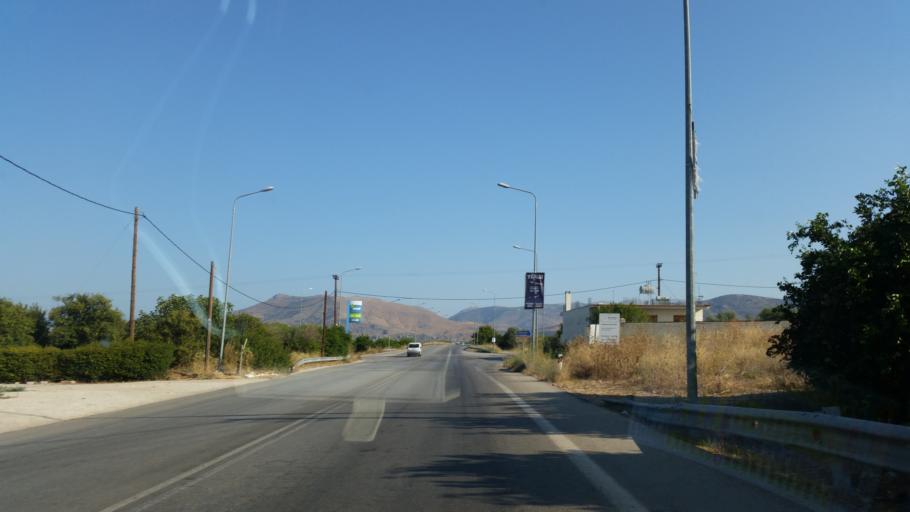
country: GR
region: Peloponnese
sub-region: Nomos Argolidos
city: Ayia Trias
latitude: 37.6325
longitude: 22.8174
